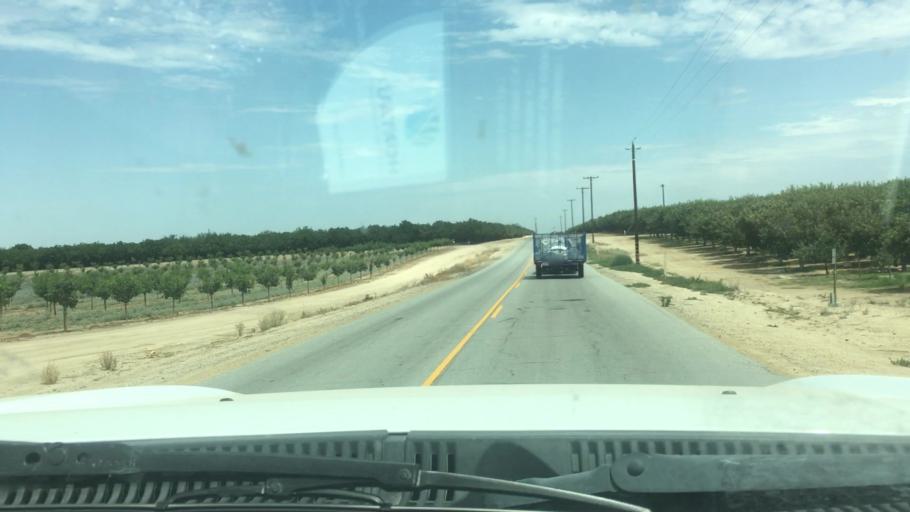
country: US
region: California
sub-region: Kern County
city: McFarland
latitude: 35.5932
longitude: -119.1510
